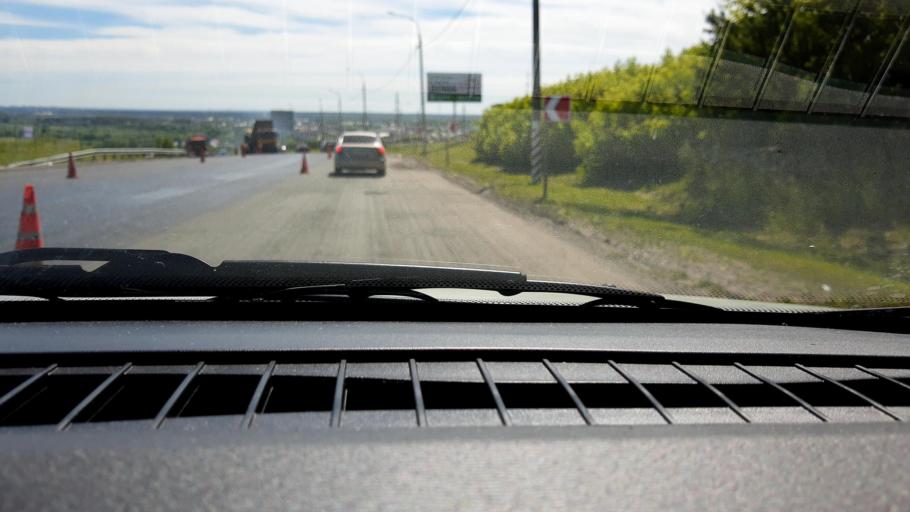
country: RU
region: Nizjnij Novgorod
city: Afonino
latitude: 56.2441
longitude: 44.0956
